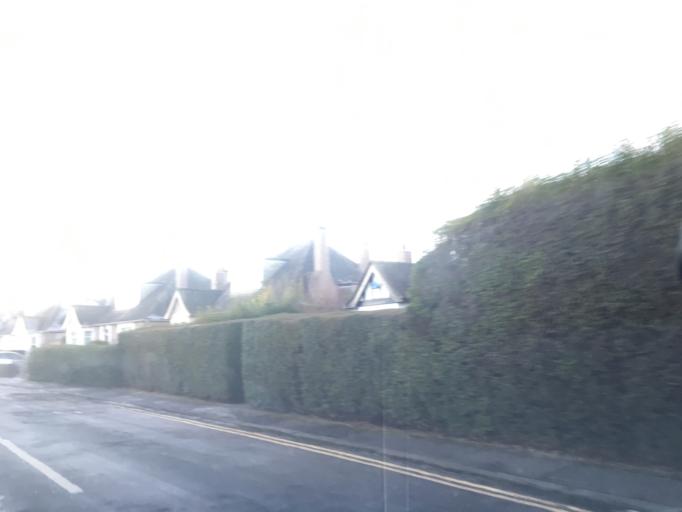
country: GB
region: Scotland
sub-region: Edinburgh
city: Edinburgh
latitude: 55.9543
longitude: -3.2358
